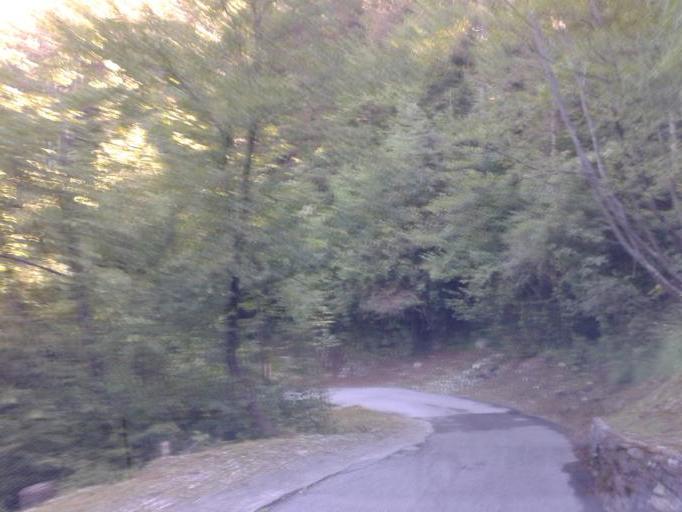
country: IT
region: Trentino-Alto Adige
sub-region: Provincia di Trento
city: Storo
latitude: 45.8511
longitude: 10.5831
